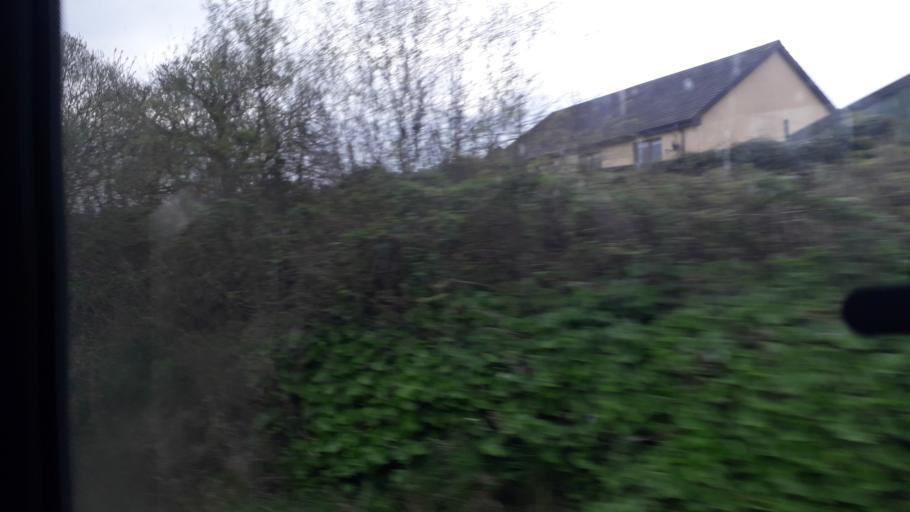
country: IE
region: Leinster
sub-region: An Longfort
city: Longford
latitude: 53.7703
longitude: -7.8312
